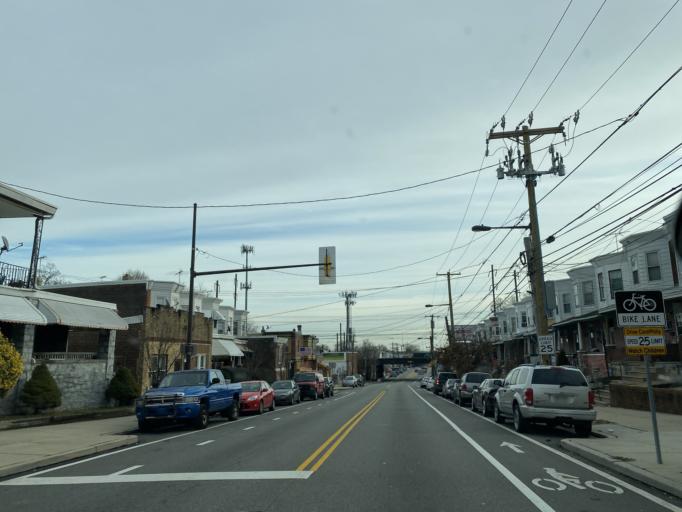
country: US
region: New Jersey
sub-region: Burlington County
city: Palmyra
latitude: 40.0262
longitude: -75.0372
